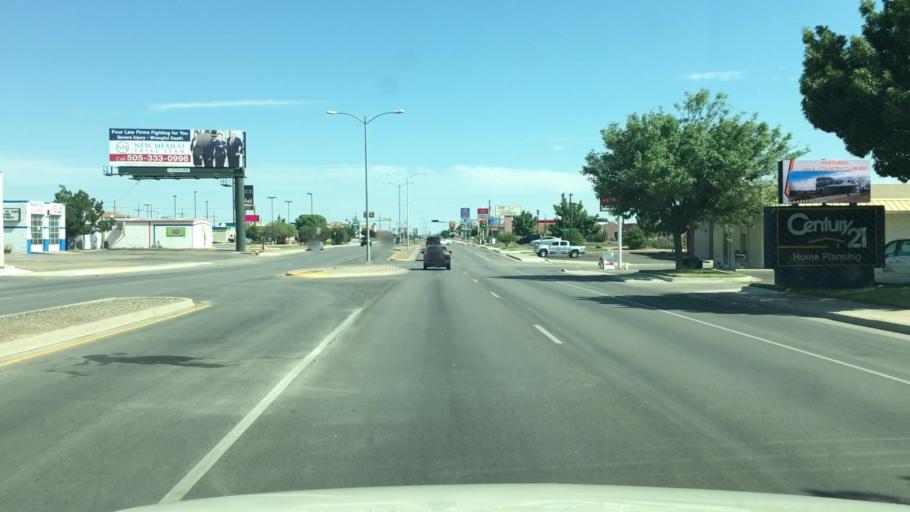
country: US
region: New Mexico
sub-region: Chaves County
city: Roswell
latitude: 33.4357
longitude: -104.5231
